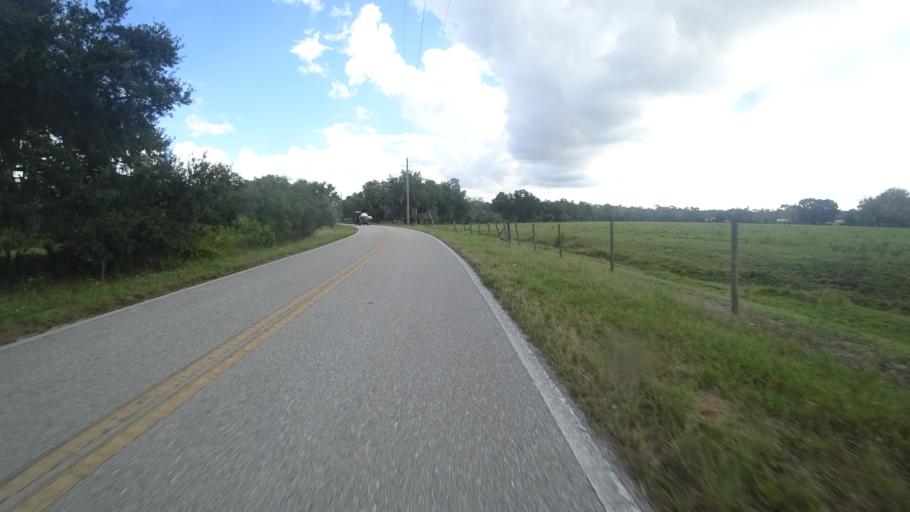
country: US
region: Florida
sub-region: Hillsborough County
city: Wimauma
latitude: 27.6054
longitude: -82.2177
